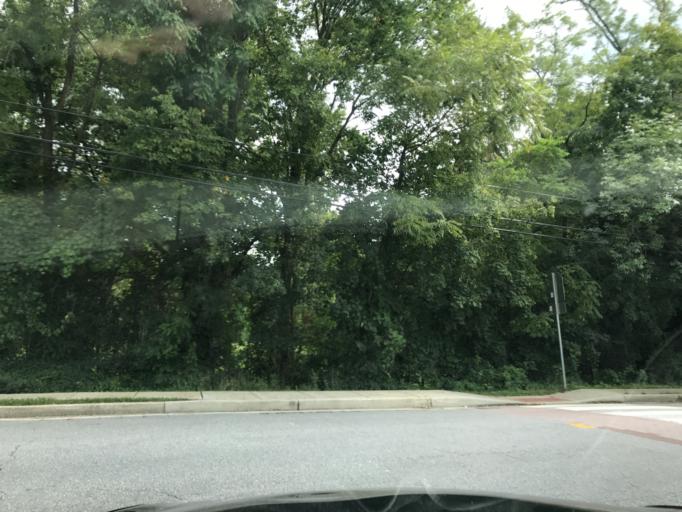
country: US
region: Maryland
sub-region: Baltimore County
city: Mays Chapel
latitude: 39.4139
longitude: -76.6473
